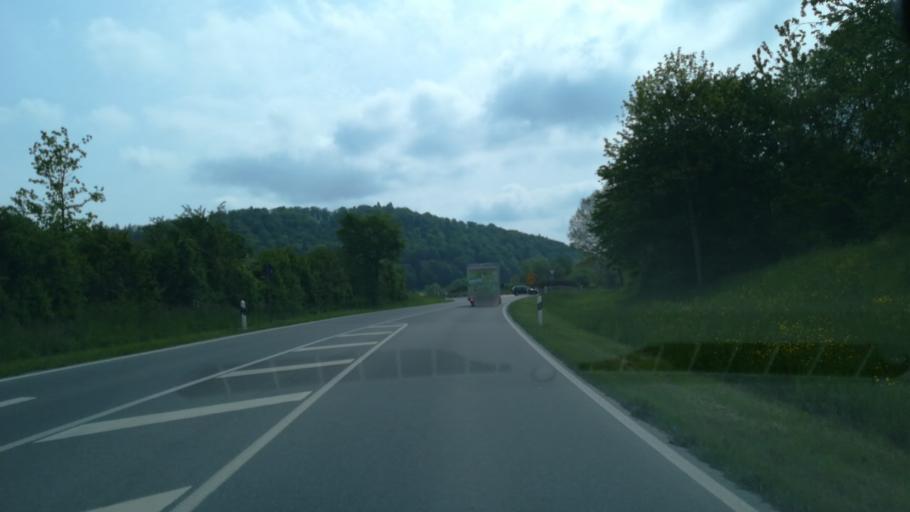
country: DE
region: Baden-Wuerttemberg
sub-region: Freiburg Region
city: Steisslingen
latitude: 47.7838
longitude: 8.9302
